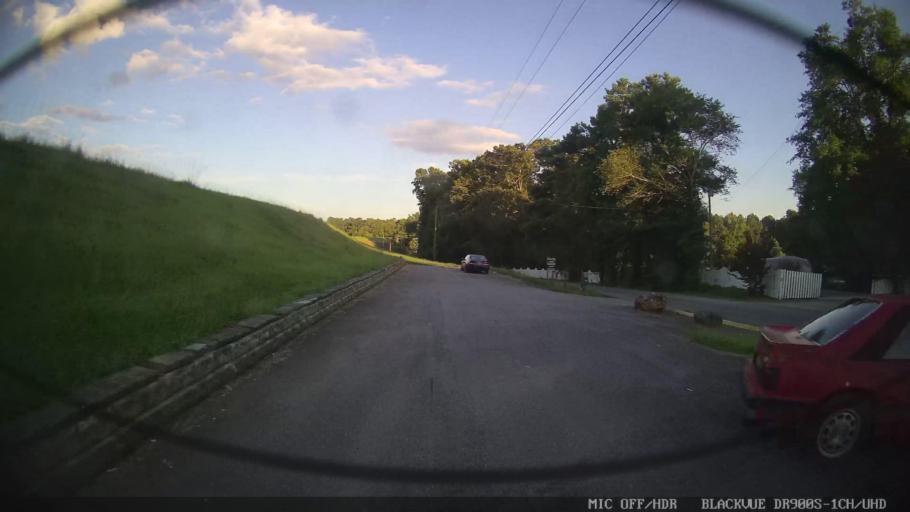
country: US
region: Georgia
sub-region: Bartow County
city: Emerson
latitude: 34.1132
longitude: -84.7140
